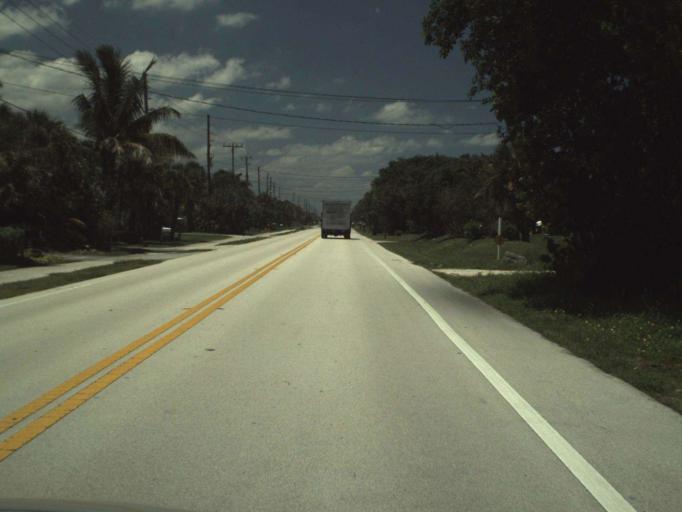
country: US
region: Florida
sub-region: Brevard County
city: Micco
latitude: 27.9134
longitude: -80.4778
